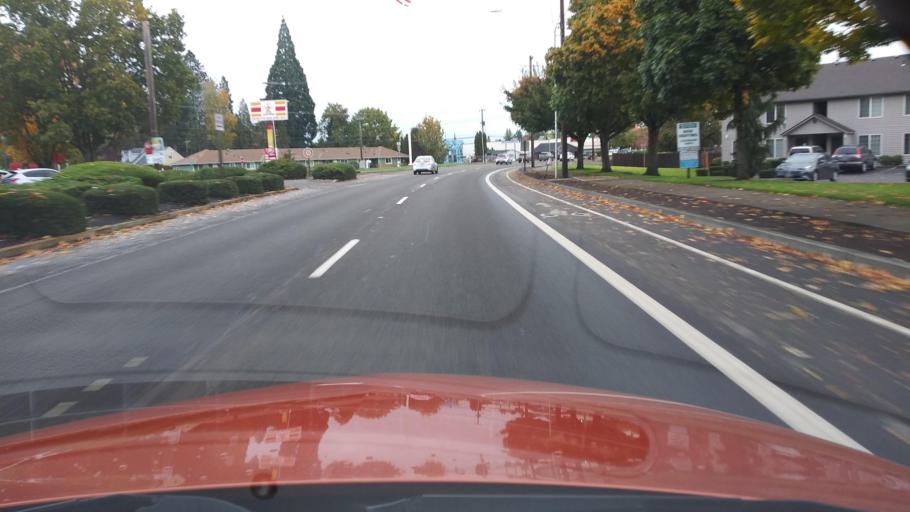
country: US
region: Oregon
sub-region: Washington County
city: Forest Grove
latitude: 45.5193
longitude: -123.0934
